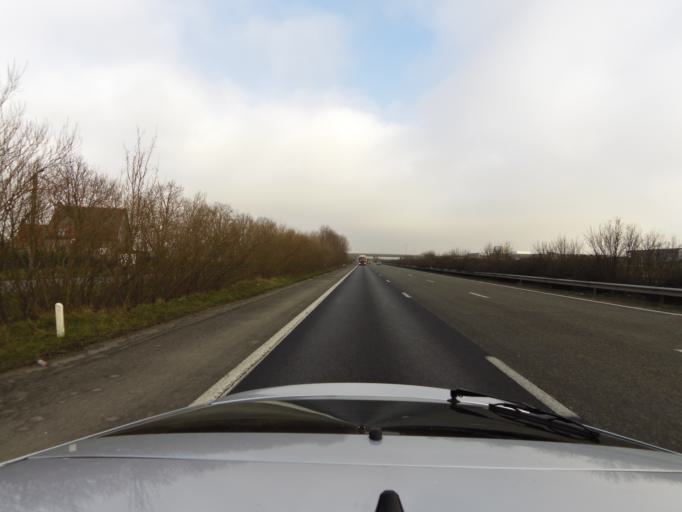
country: BE
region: Flanders
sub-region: Provincie West-Vlaanderen
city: Wevelgem
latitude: 50.8484
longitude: 3.1735
